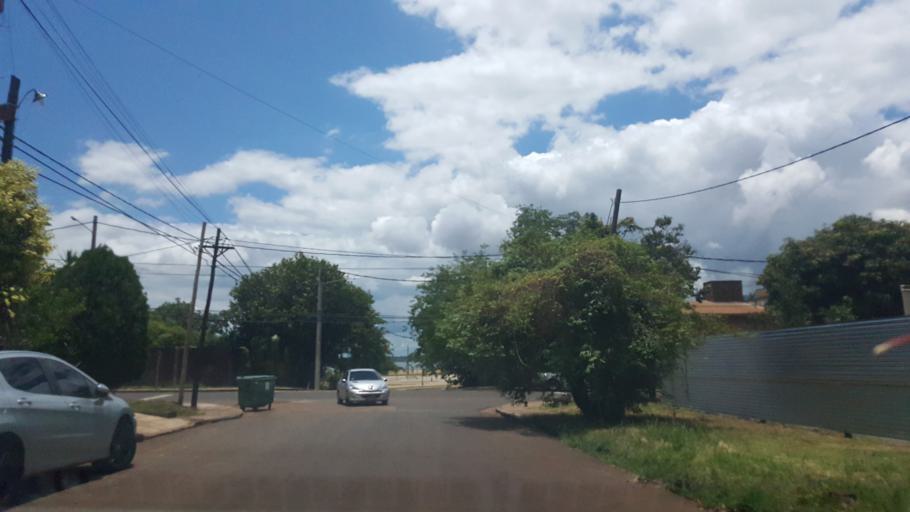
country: AR
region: Misiones
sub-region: Departamento de Capital
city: Posadas
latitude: -27.3541
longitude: -55.9008
